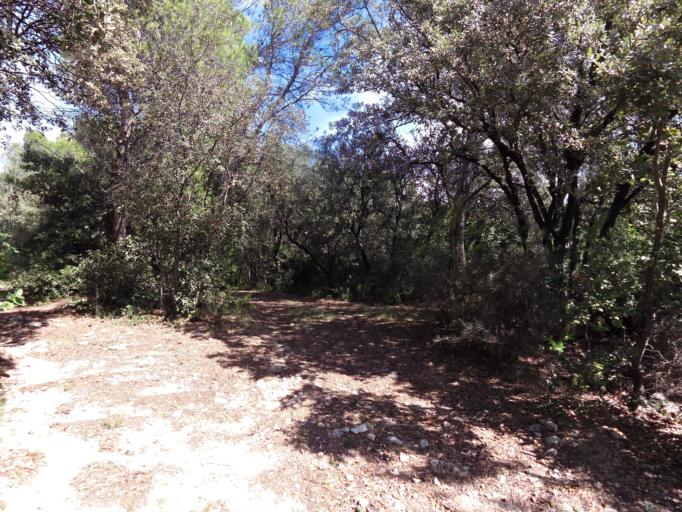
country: FR
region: Languedoc-Roussillon
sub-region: Departement du Gard
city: Mus
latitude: 43.7460
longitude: 4.1979
